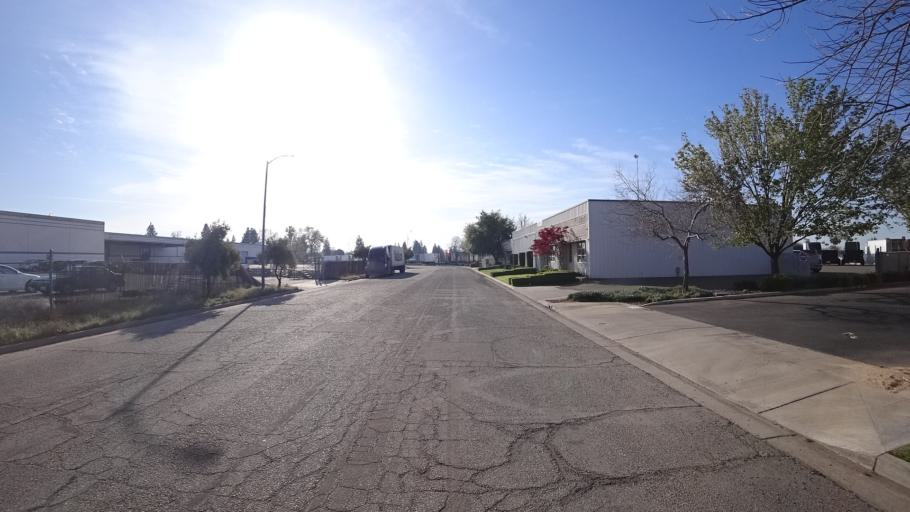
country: US
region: California
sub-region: Fresno County
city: West Park
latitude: 36.8143
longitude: -119.8832
